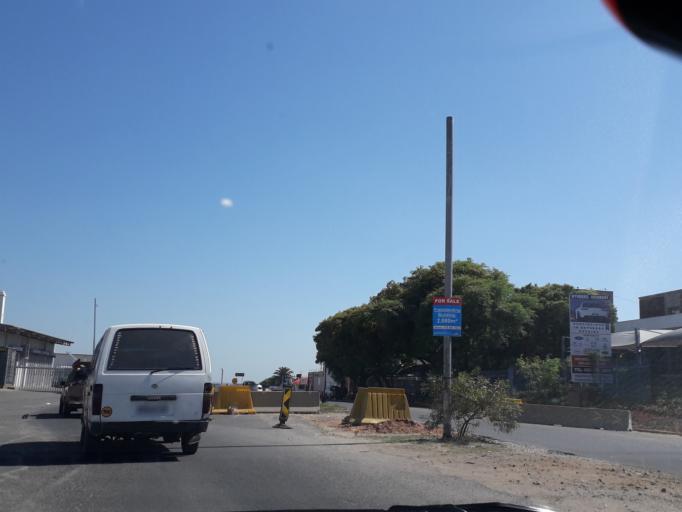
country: ZA
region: Gauteng
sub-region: City of Johannesburg Metropolitan Municipality
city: Modderfontein
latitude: -26.1155
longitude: 28.0844
